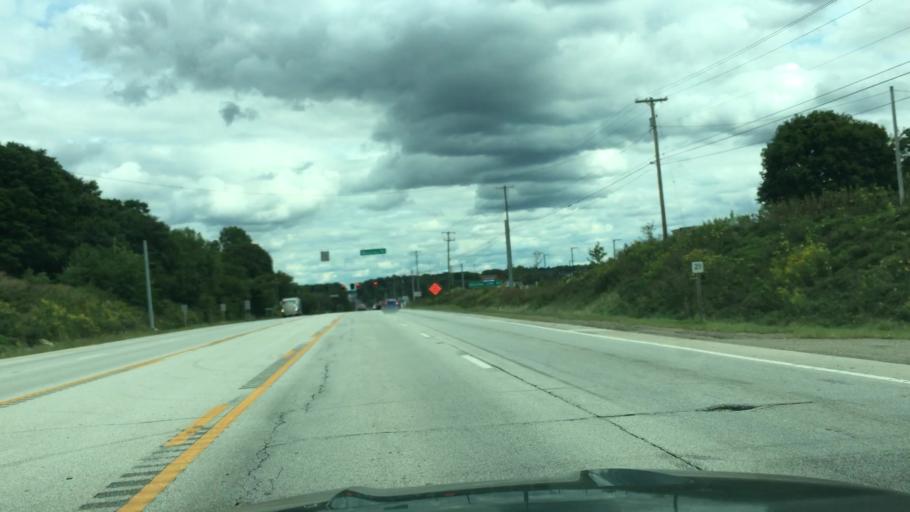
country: US
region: Ohio
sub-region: Summit County
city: Montrose-Ghent
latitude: 41.1359
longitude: -81.6895
